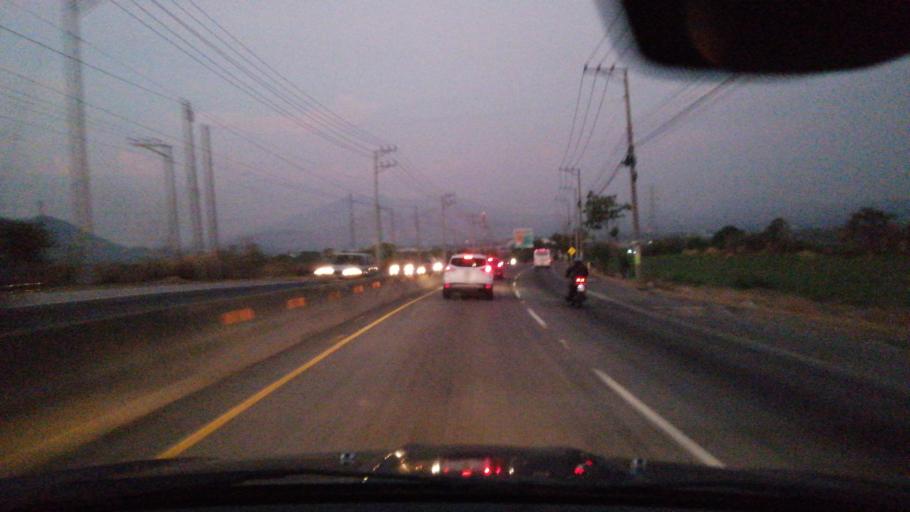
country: SV
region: San Salvador
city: Ayutuxtepeque
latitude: 13.7709
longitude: -89.2116
